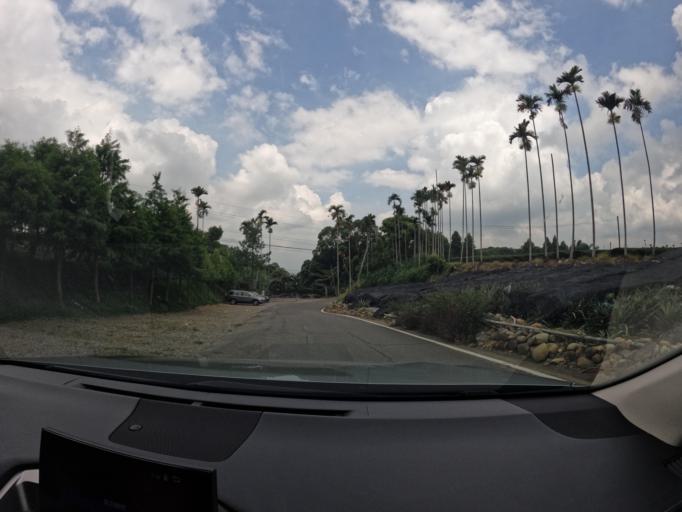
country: TW
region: Taiwan
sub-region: Nantou
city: Nantou
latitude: 23.9093
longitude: 120.6337
